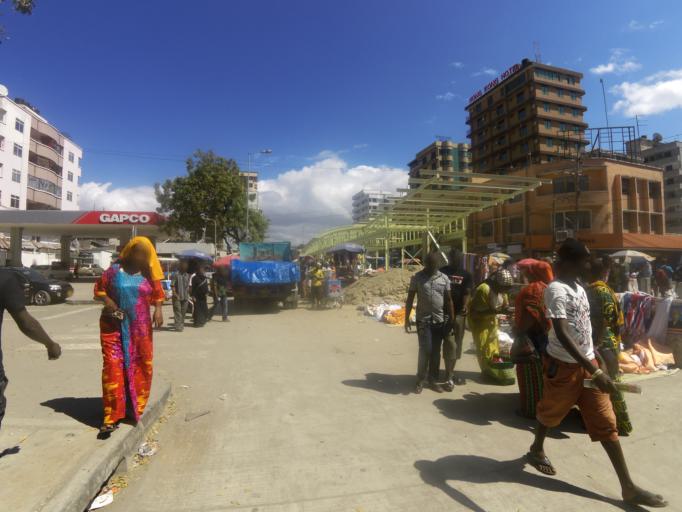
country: TZ
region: Dar es Salaam
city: Dar es Salaam
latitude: -6.8207
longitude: 39.2729
